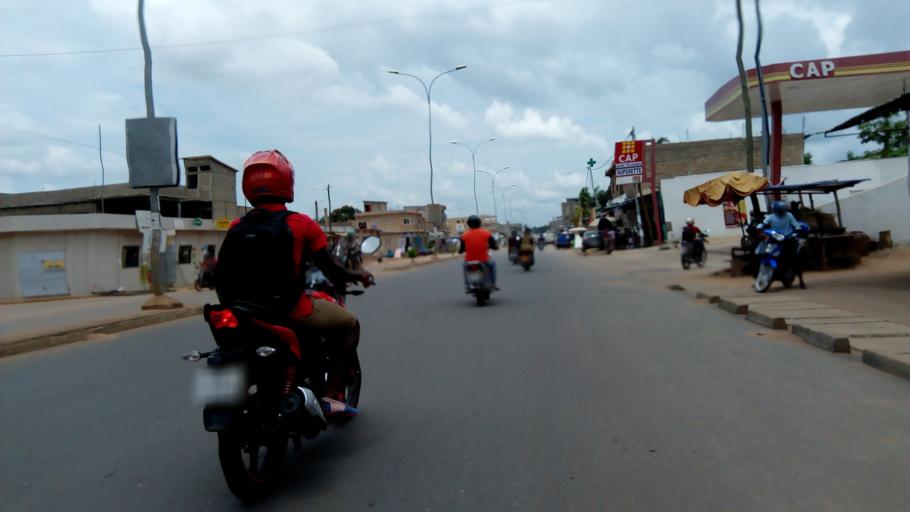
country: TG
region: Maritime
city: Lome
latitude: 6.2154
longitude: 1.1727
